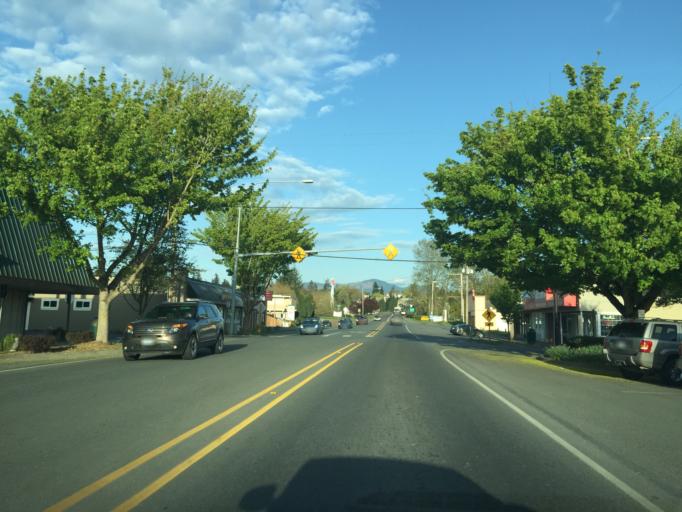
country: US
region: Washington
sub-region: Skagit County
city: Mount Vernon
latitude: 48.4217
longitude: -122.3441
